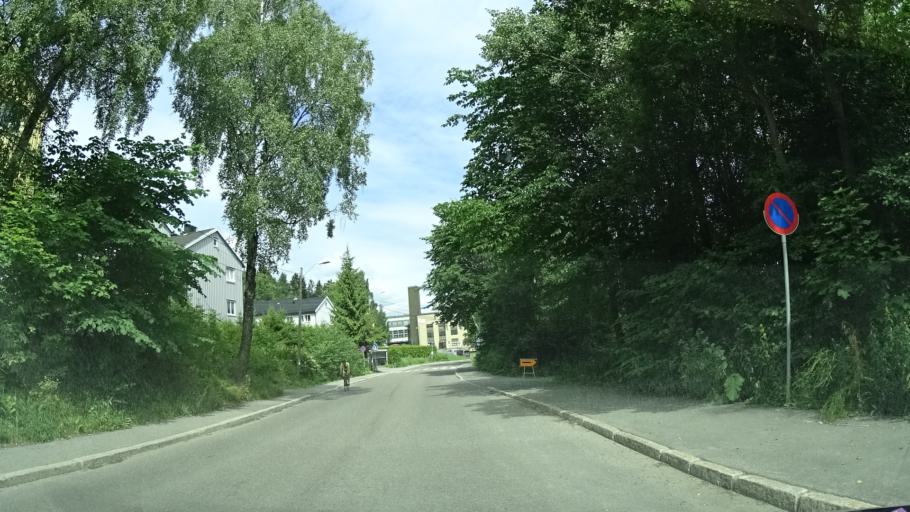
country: NO
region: Oslo
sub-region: Oslo
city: Oslo
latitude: 59.9624
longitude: 10.7691
